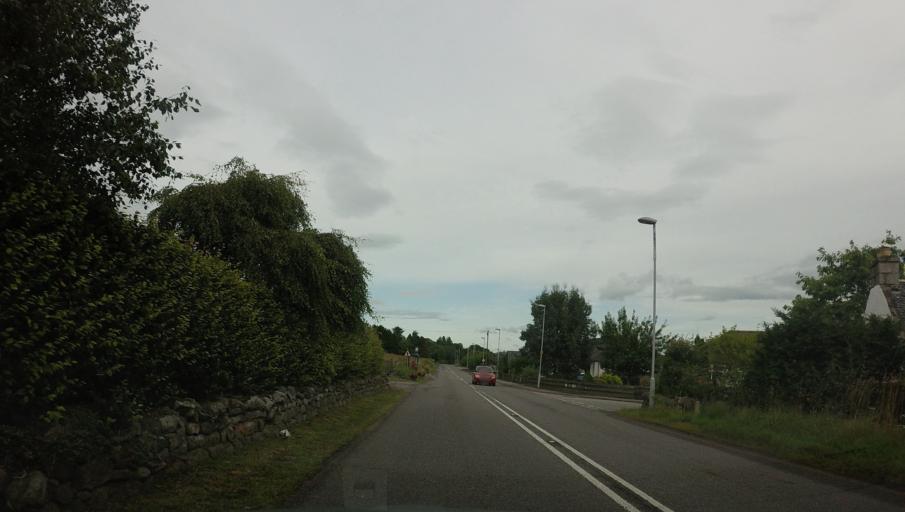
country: GB
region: Scotland
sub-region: Aberdeenshire
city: Banchory
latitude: 57.0613
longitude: -2.5608
